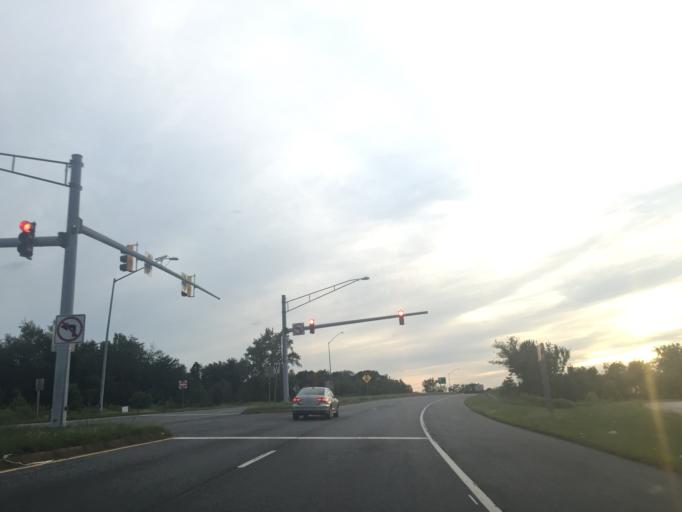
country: US
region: Maryland
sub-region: Anne Arundel County
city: Brooklyn Park
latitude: 39.1941
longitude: -76.6006
